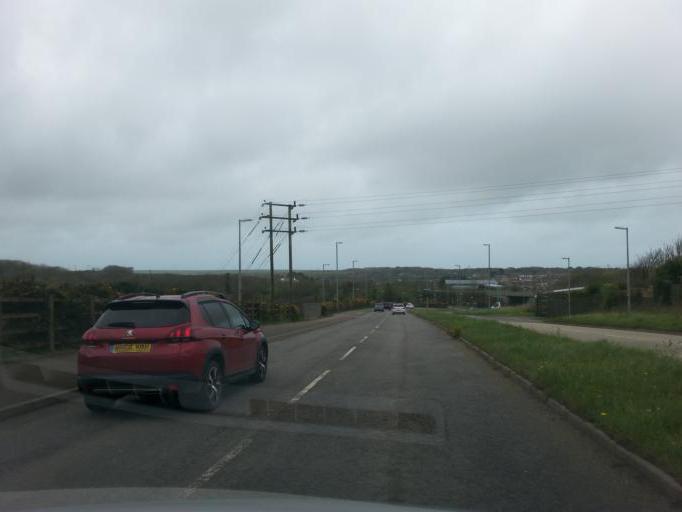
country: GB
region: England
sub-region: Cornwall
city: Camborne
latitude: 50.2270
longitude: -5.2805
